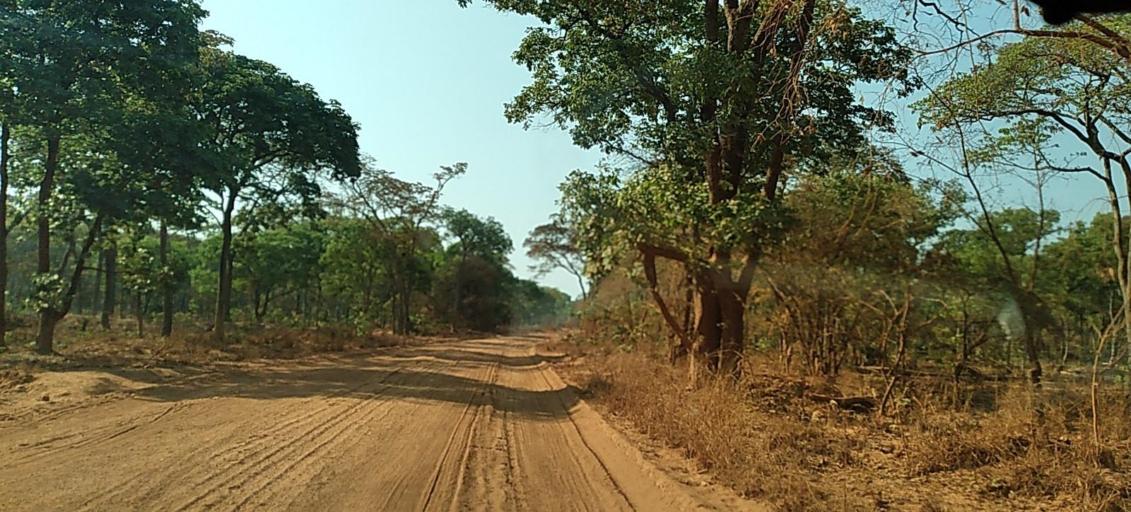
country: ZM
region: North-Western
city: Kasempa
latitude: -13.6848
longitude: 26.0270
